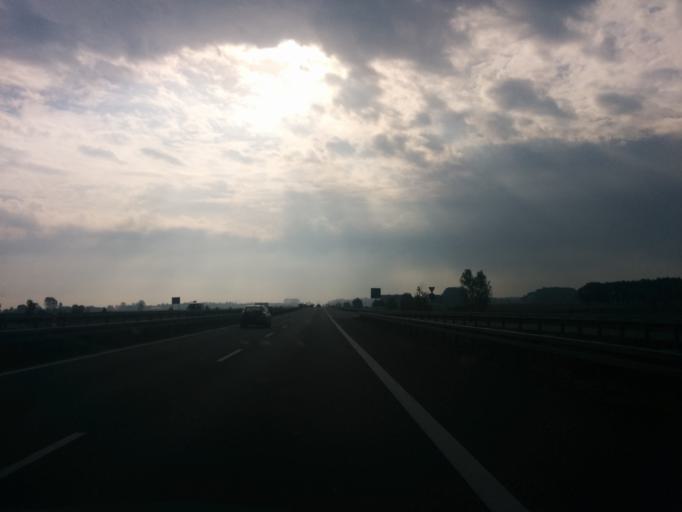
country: PL
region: Masovian Voivodeship
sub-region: Powiat radomski
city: Jedlinsk
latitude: 51.5420
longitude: 21.0607
